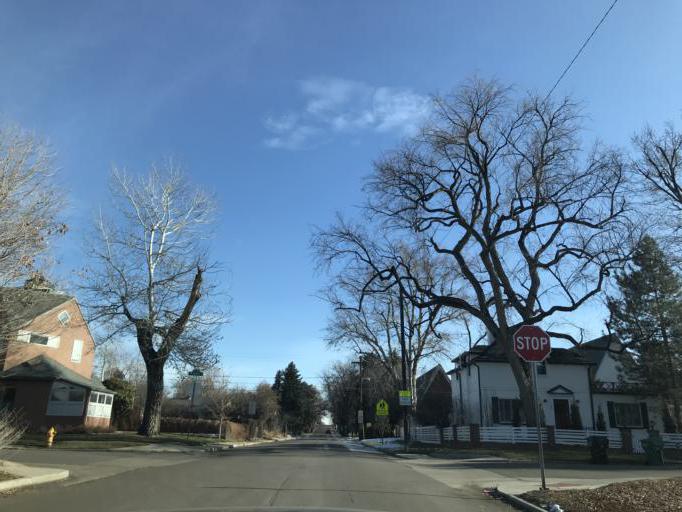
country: US
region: Colorado
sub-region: Arapahoe County
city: Glendale
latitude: 39.7357
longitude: -104.9108
